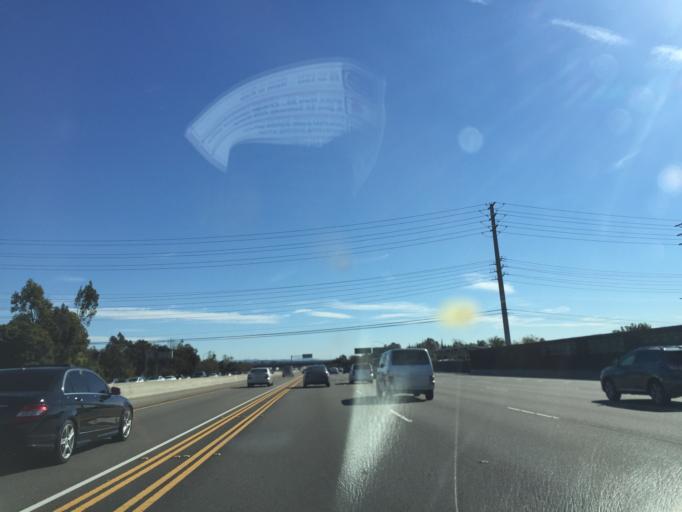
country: US
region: California
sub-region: Orange County
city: Tustin
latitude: 33.7295
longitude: -117.8096
